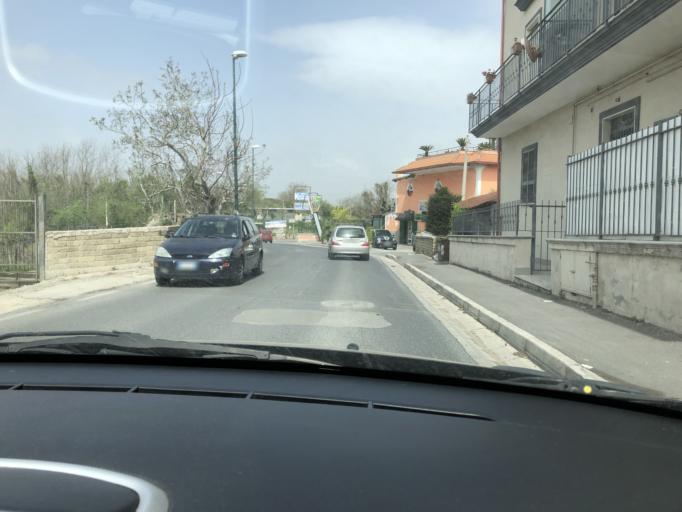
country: IT
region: Campania
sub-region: Provincia di Napoli
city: Torre Caracciolo
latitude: 40.8748
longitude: 14.1867
